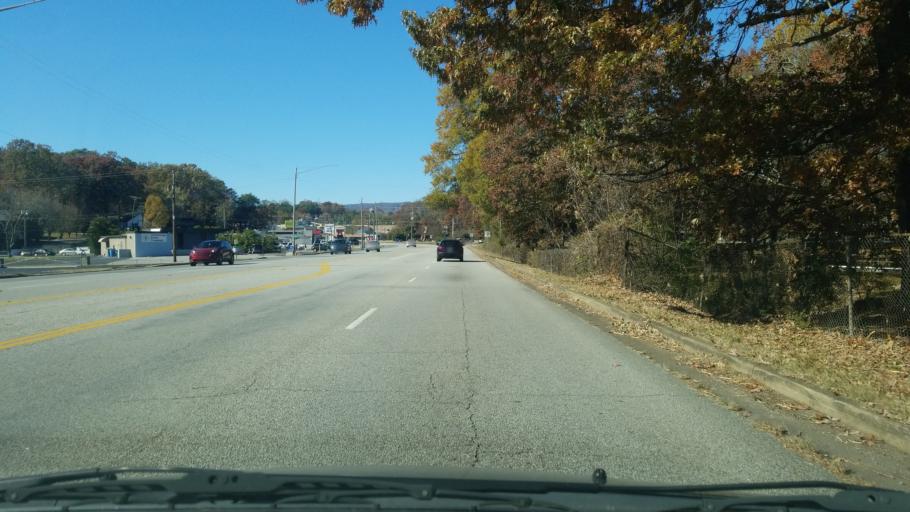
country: US
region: Tennessee
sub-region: Hamilton County
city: Red Bank
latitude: 35.1133
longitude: -85.2546
